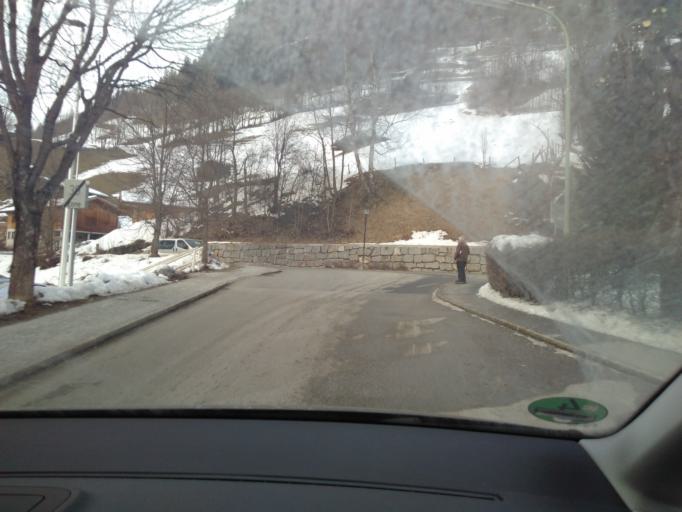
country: AT
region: Salzburg
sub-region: Politischer Bezirk Sankt Johann im Pongau
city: Bad Hofgastein
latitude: 47.1789
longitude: 13.1032
